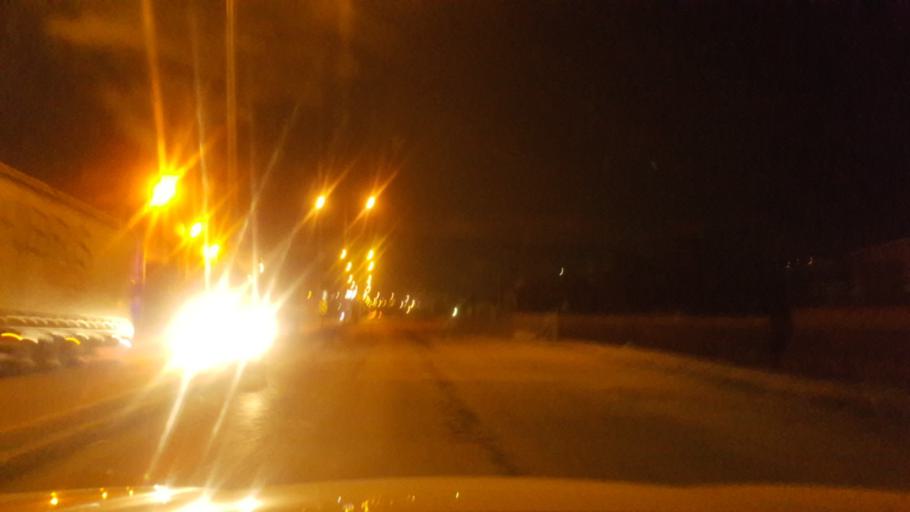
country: TR
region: Kocaeli
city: Tavsanli
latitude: 40.7825
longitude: 29.5299
